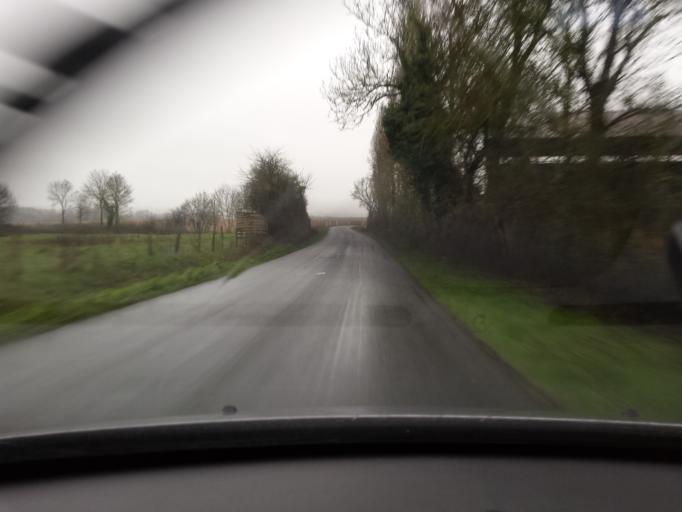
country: FR
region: Pays de la Loire
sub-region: Departement de la Vendee
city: Bournezeau
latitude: 46.5868
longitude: -1.1527
